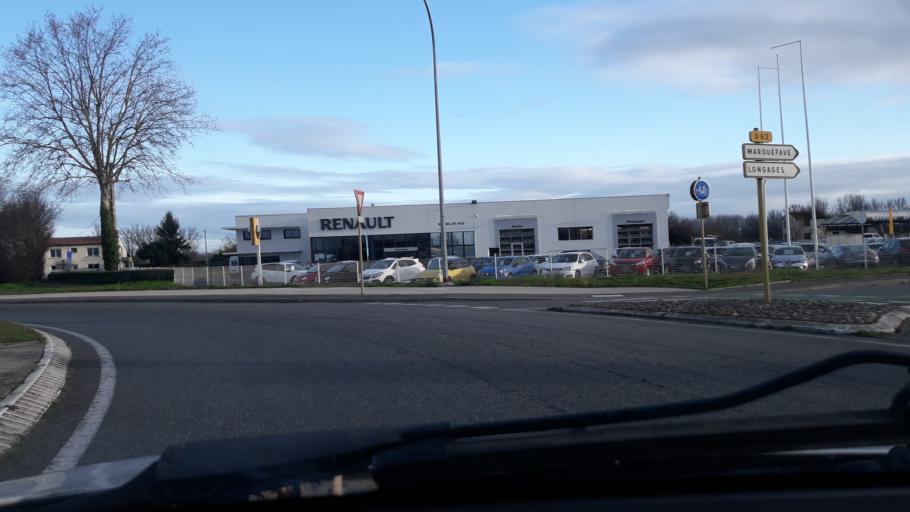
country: FR
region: Midi-Pyrenees
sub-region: Departement de la Haute-Garonne
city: Carbonne
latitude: 43.3100
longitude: 1.2230
